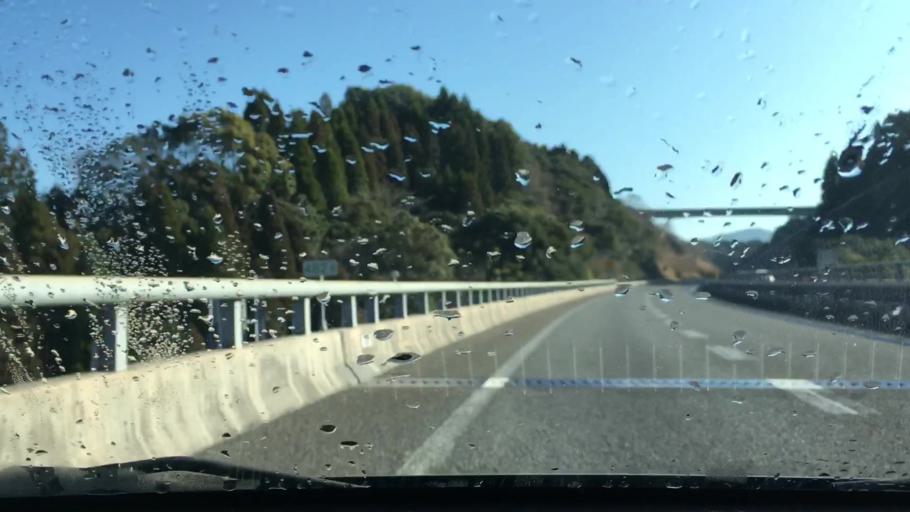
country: JP
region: Kagoshima
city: Kokubu-matsuki
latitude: 31.7429
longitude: 130.7991
